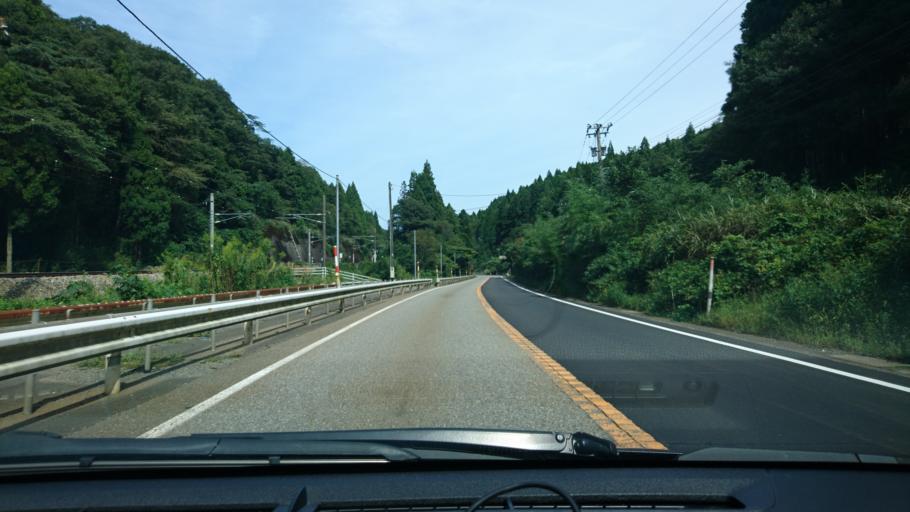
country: JP
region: Fukui
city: Maruoka
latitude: 36.2730
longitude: 136.2895
